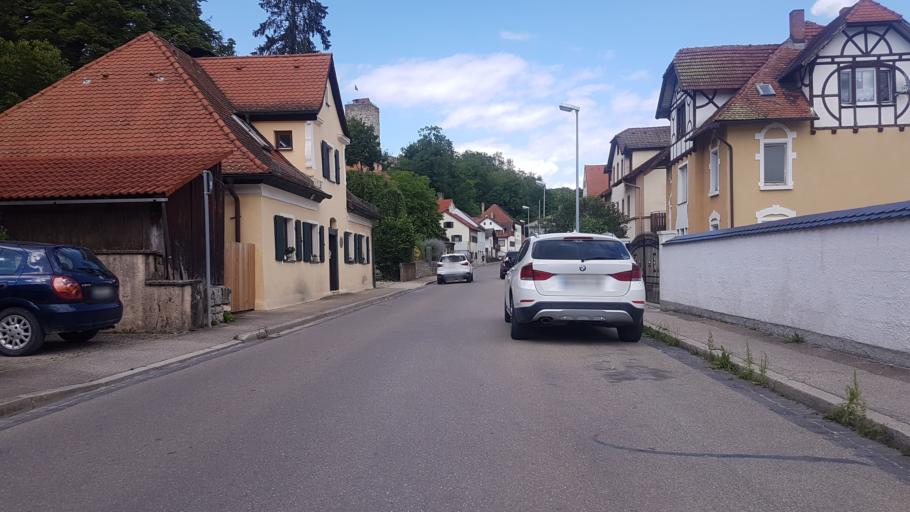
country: DE
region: Bavaria
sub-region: Regierungsbezirk Mittelfranken
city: Pappenheim
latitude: 48.9305
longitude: 10.9692
